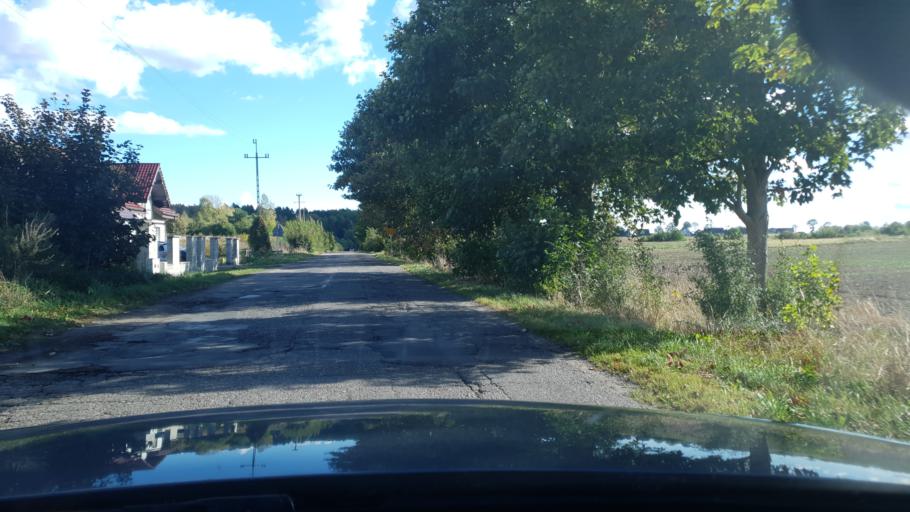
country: PL
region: Pomeranian Voivodeship
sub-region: Powiat pucki
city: Zelistrzewo
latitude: 54.6906
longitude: 18.4184
